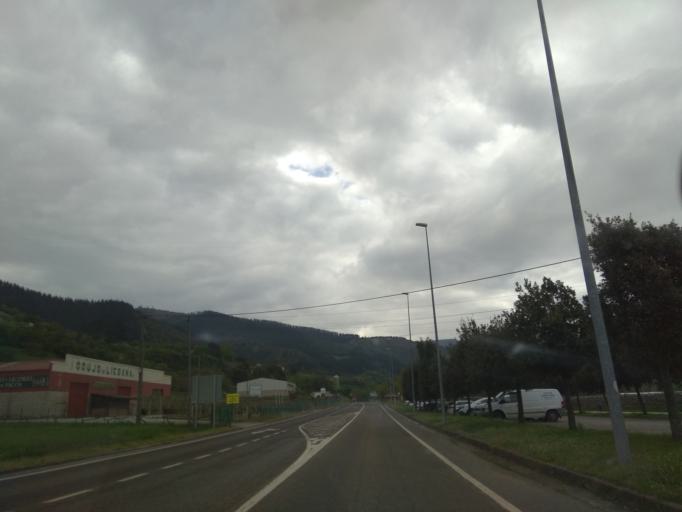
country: ES
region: Cantabria
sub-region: Provincia de Cantabria
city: Potes
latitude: 43.1826
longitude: -4.6014
